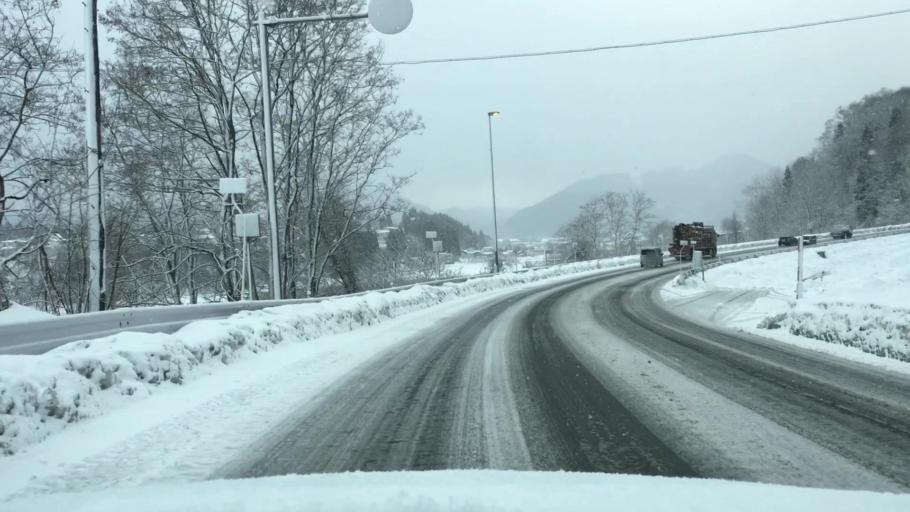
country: JP
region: Aomori
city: Kuroishi
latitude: 40.4955
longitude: 140.6172
